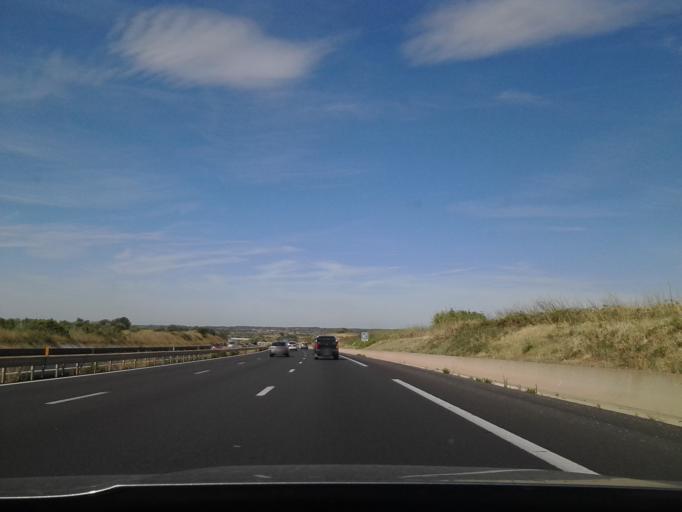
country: FR
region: Languedoc-Roussillon
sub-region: Departement de l'Herault
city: Loupian
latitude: 43.4609
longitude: 3.6193
